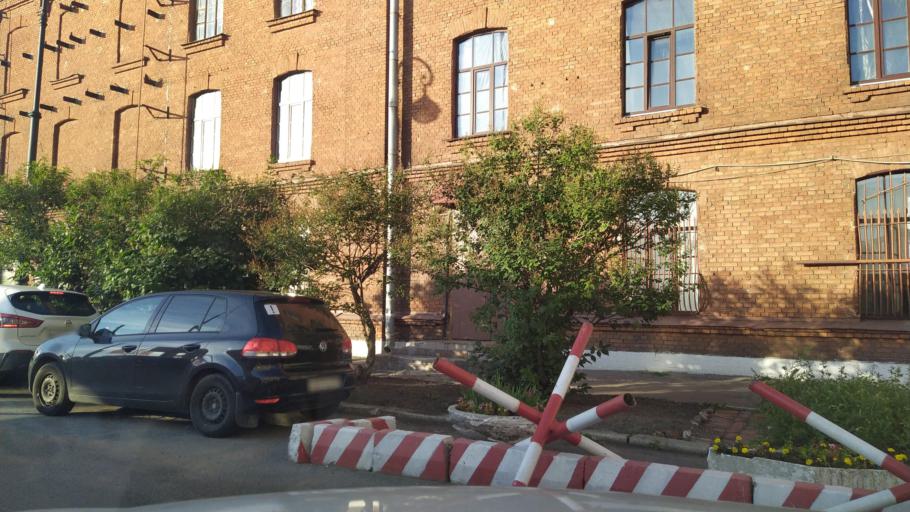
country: RU
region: St.-Petersburg
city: Vasyl'evsky Ostrov
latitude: 59.9265
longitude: 30.2414
